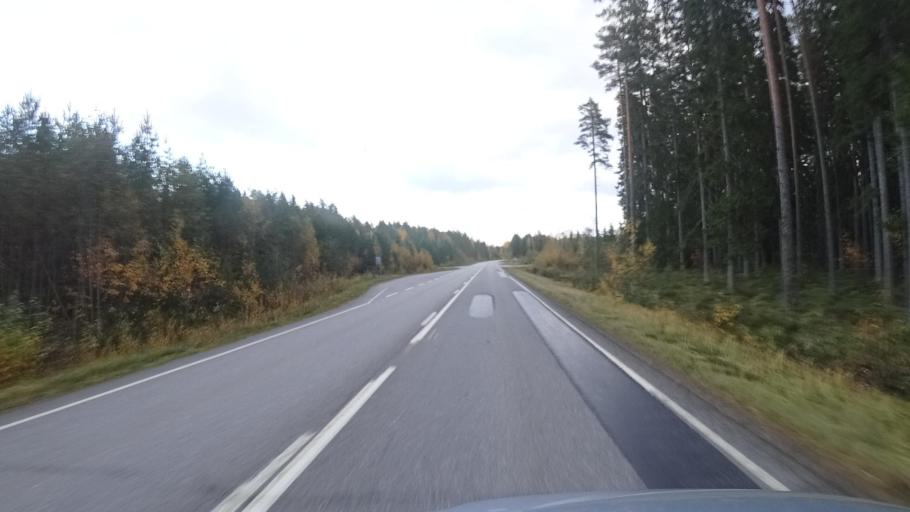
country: FI
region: Varsinais-Suomi
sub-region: Loimaa
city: Ylaene
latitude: 60.9967
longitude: 22.4884
